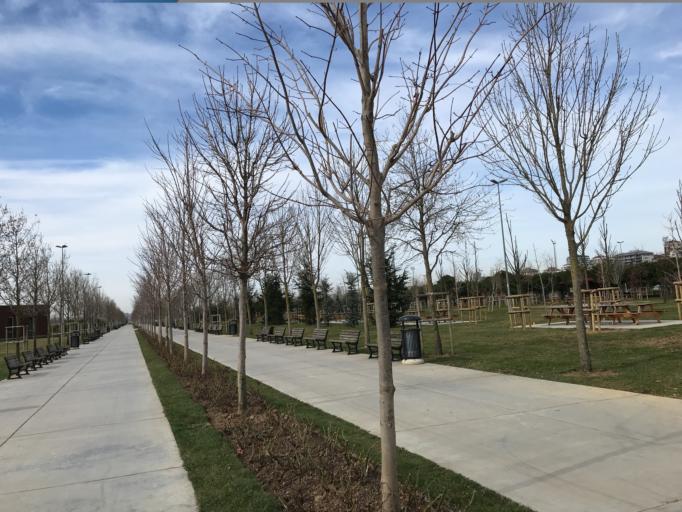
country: TR
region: Istanbul
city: Maltepe
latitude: 40.9262
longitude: 29.1178
